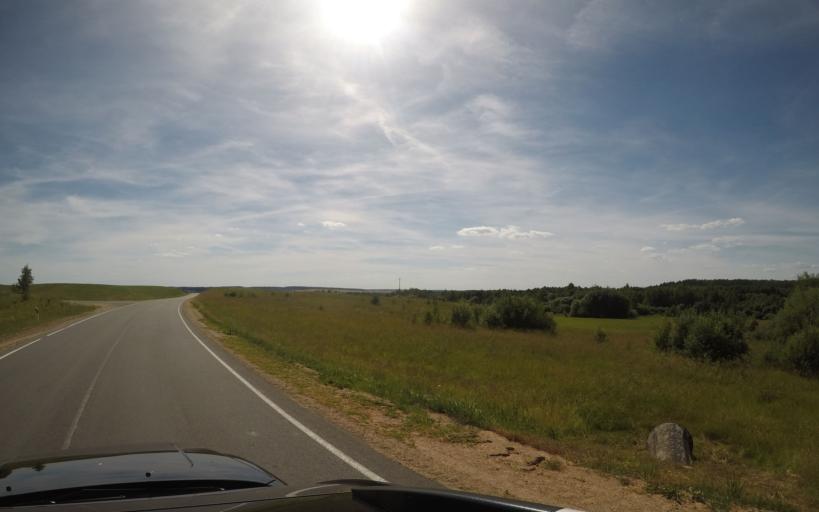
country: BY
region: Grodnenskaya
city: Hal'shany
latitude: 54.2674
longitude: 26.0298
